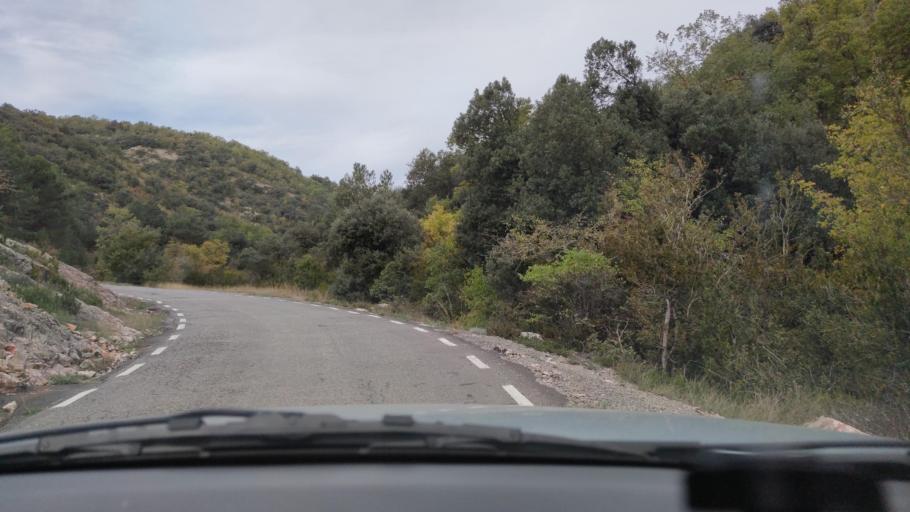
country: ES
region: Catalonia
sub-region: Provincia de Lleida
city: Llimiana
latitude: 42.0335
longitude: 1.0233
